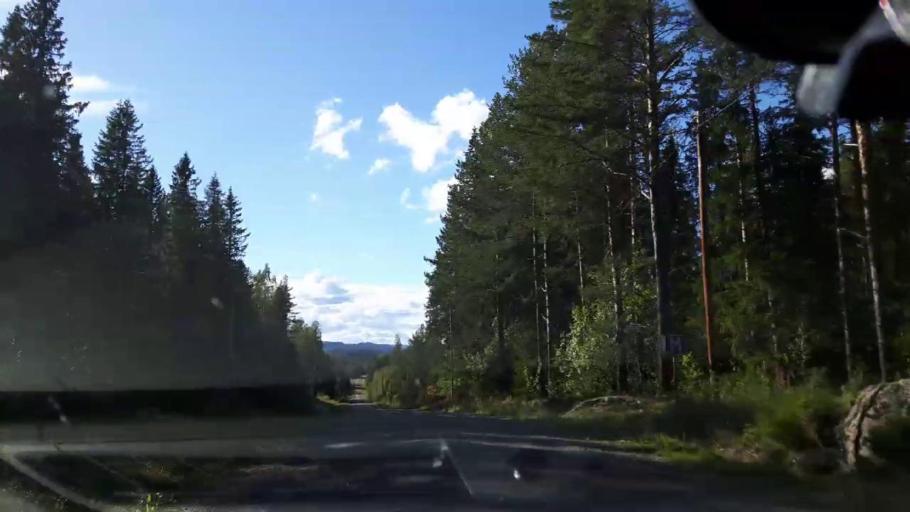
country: SE
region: Vaesternorrland
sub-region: Solleftea Kommun
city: As
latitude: 63.4627
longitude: 16.2506
